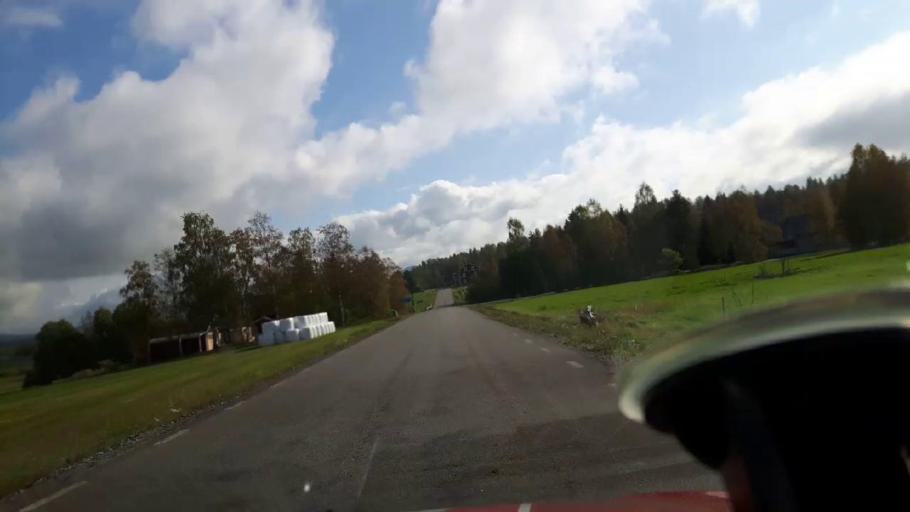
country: SE
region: Gaevleborg
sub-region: Ljusdals Kommun
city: Jaervsoe
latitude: 61.7539
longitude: 16.1313
